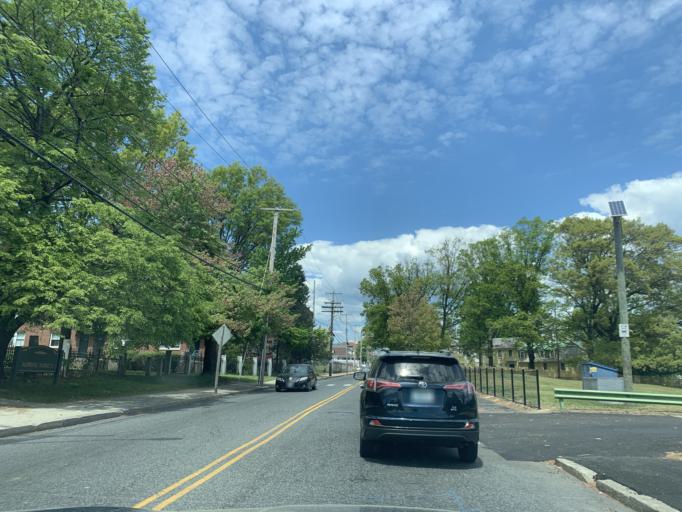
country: US
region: Rhode Island
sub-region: Providence County
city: Providence
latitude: 41.8409
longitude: -71.4199
